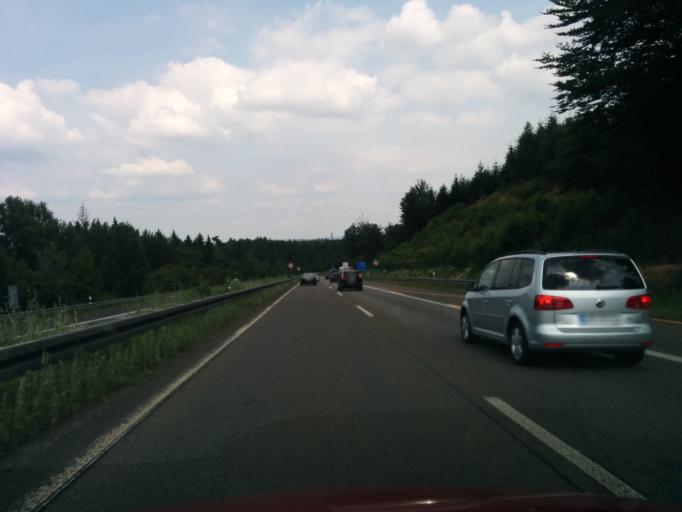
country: DE
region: Hesse
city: Grebenau
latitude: 50.7957
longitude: 9.4810
